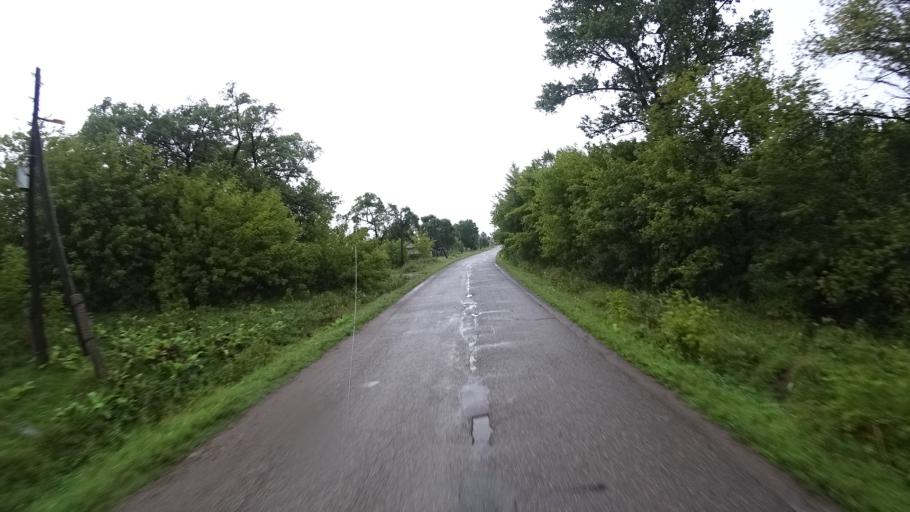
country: RU
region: Primorskiy
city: Monastyrishche
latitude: 44.2674
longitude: 132.4203
